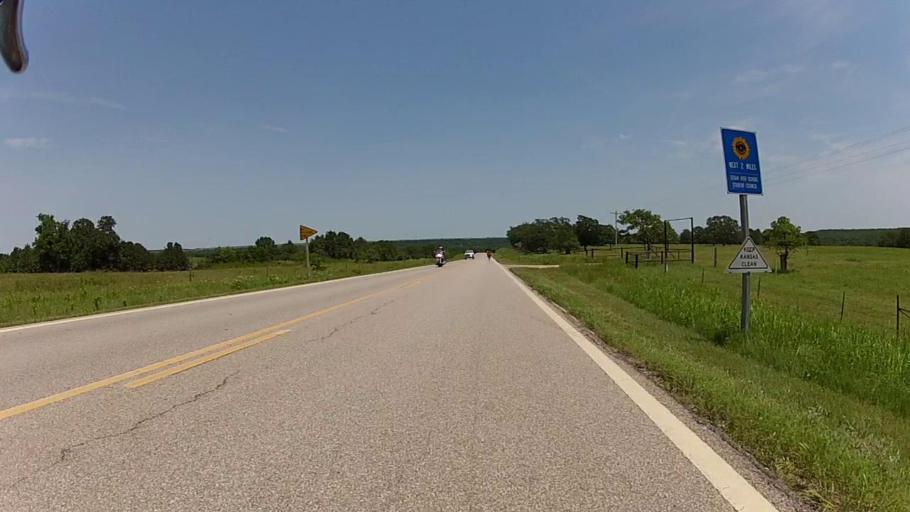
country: US
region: Kansas
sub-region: Chautauqua County
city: Sedan
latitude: 37.1170
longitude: -96.2395
